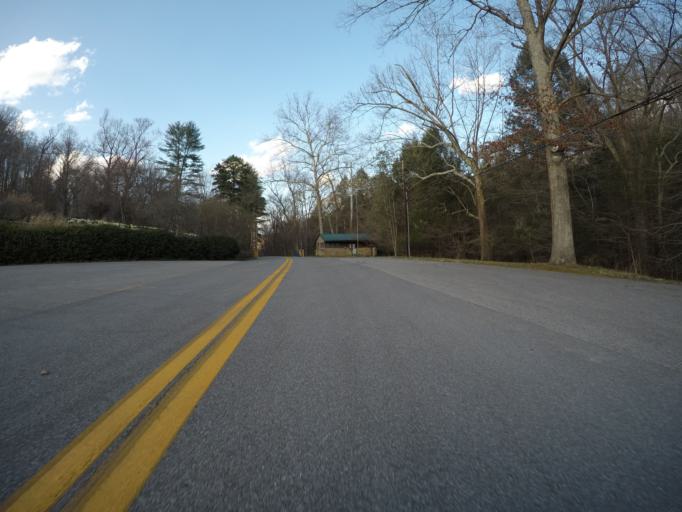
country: US
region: West Virginia
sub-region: Kanawha County
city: Charleston
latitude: 38.3769
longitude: -81.5833
